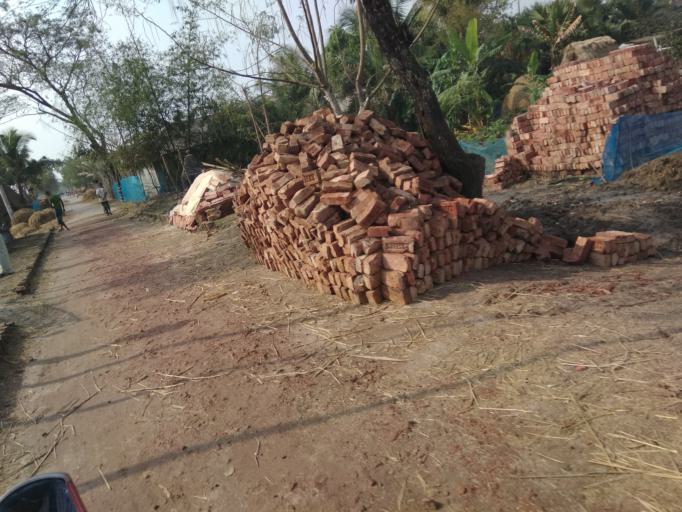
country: IN
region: West Bengal
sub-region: North 24 Parganas
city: Gosaba
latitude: 22.2621
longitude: 89.1154
